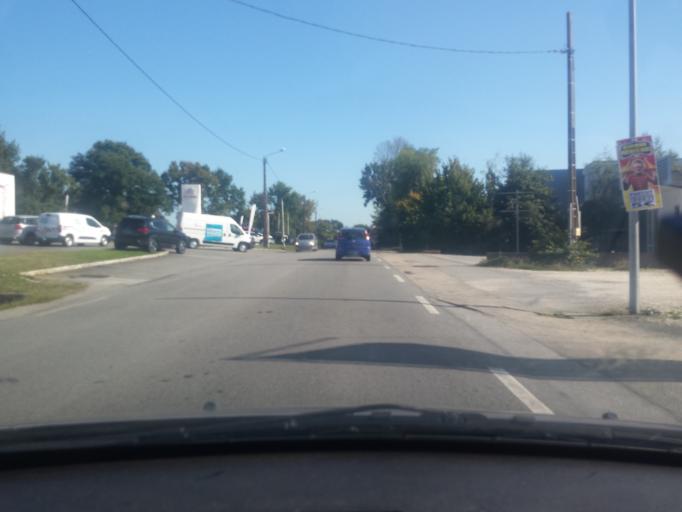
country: FR
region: Brittany
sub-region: Departement du Morbihan
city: Pontivy
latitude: 48.0601
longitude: -2.9550
